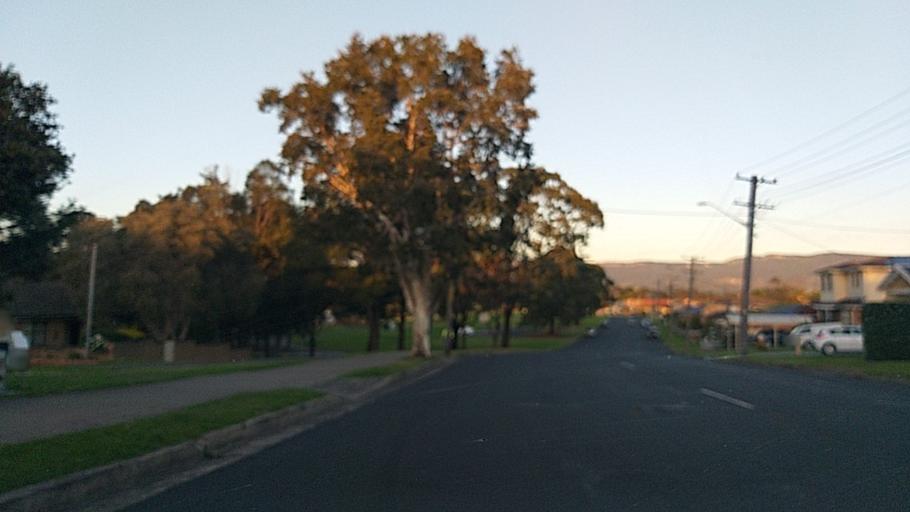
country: AU
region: New South Wales
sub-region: Wollongong
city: Koonawarra
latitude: -34.5000
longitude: 150.8210
